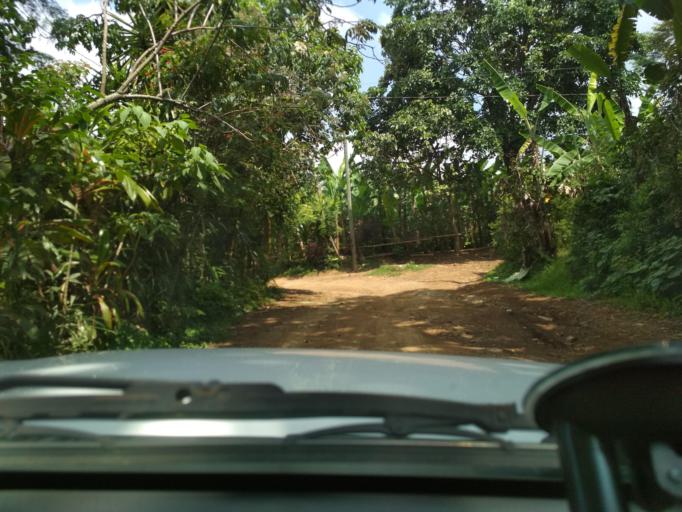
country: MX
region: Veracruz
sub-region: Fortin
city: Santa Lucia Potrerillo
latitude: 18.9678
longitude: -97.0263
